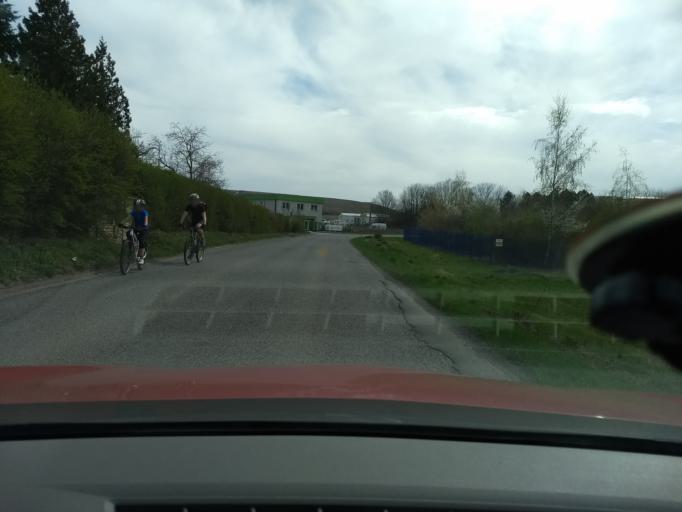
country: CZ
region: Central Bohemia
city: Hostivice
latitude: 50.0644
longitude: 14.2373
